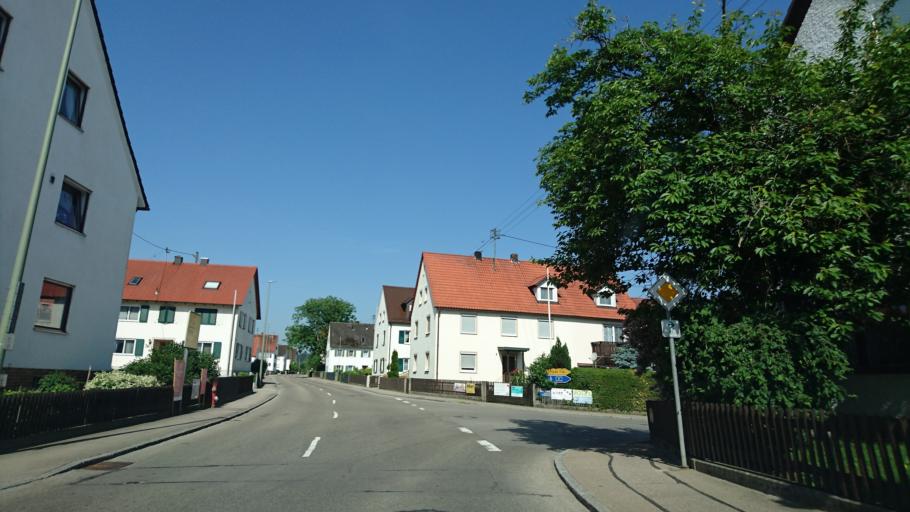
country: DE
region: Bavaria
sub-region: Swabia
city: Kutzenhausen
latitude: 48.3615
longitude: 10.6853
